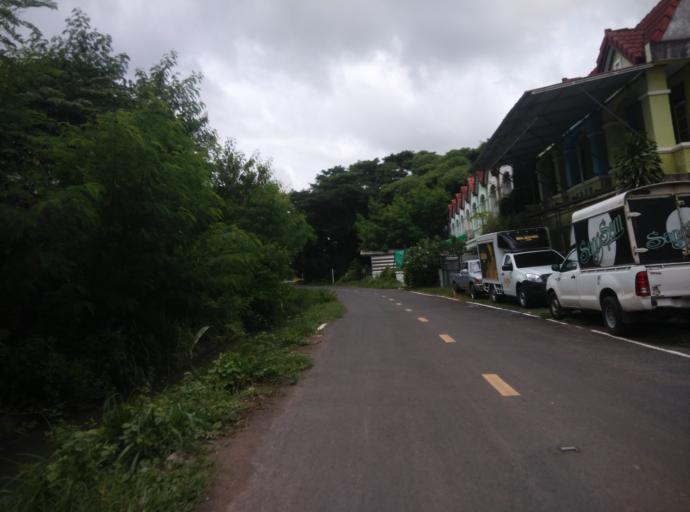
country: TH
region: Sisaket
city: Si Sa Ket
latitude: 15.1101
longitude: 104.3428
